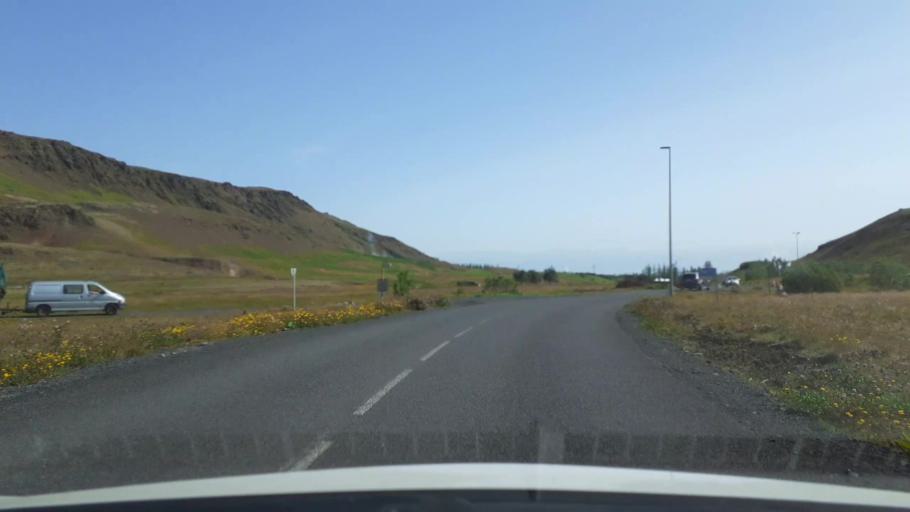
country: IS
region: South
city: Hveragerdi
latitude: 64.0120
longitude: -21.1919
